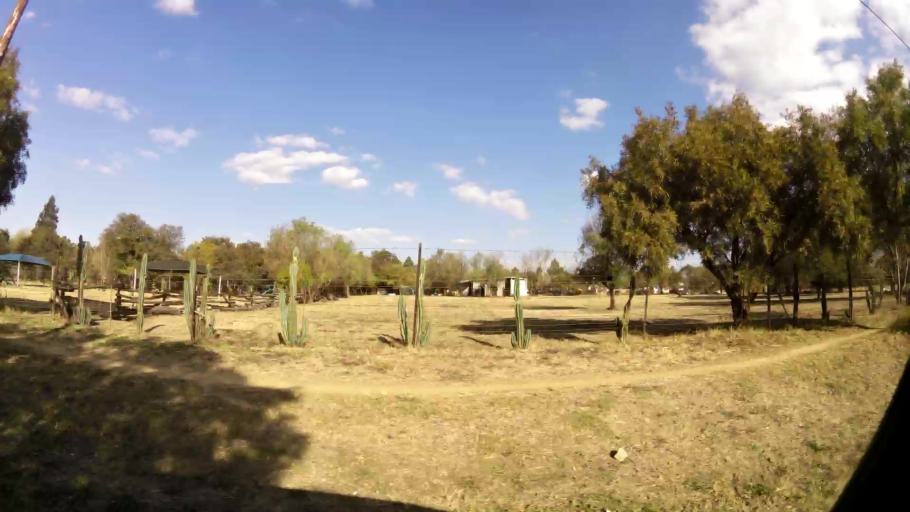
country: ZA
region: Gauteng
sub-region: City of Johannesburg Metropolitan Municipality
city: Midrand
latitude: -26.0208
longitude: 28.1468
